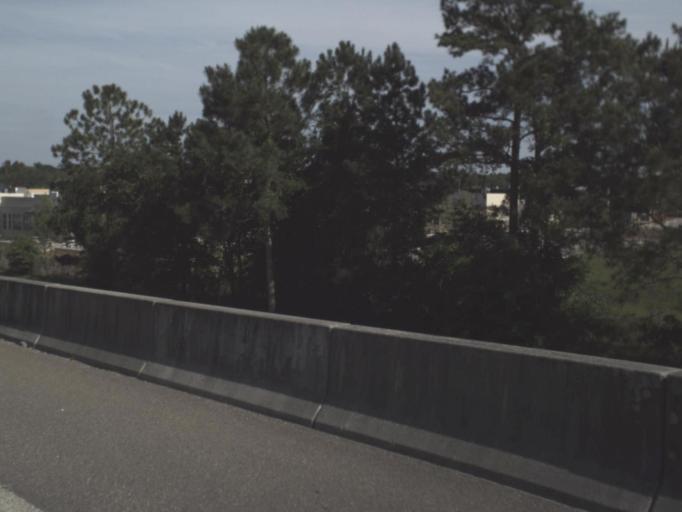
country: US
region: Florida
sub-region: Duval County
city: Jacksonville
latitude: 30.2510
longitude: -81.5811
